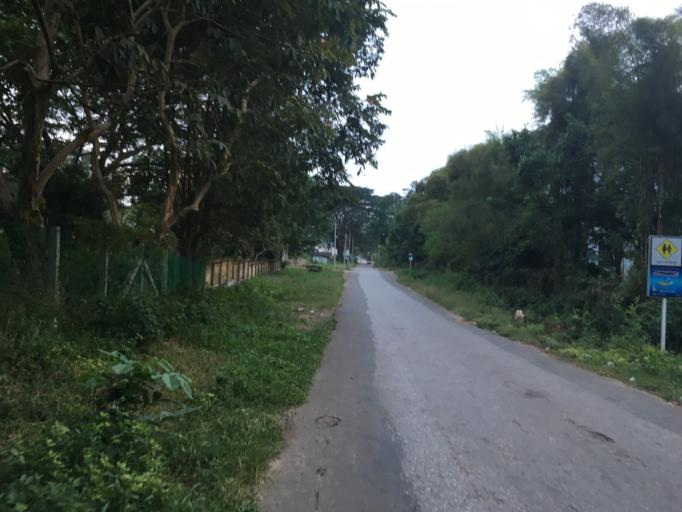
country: MM
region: Mon
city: Mawlamyine
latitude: 16.4783
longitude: 97.6264
